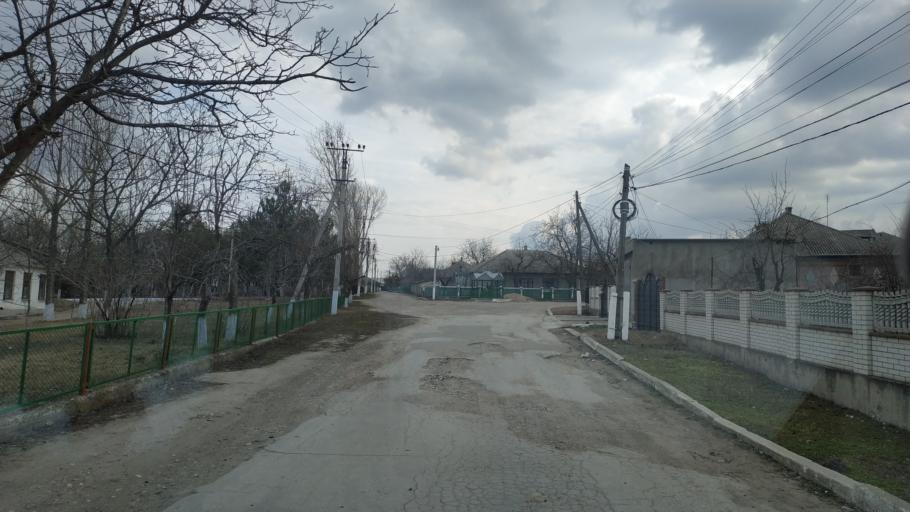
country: MD
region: Anenii Noi
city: Anenii Noi
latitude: 46.8842
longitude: 29.3104
